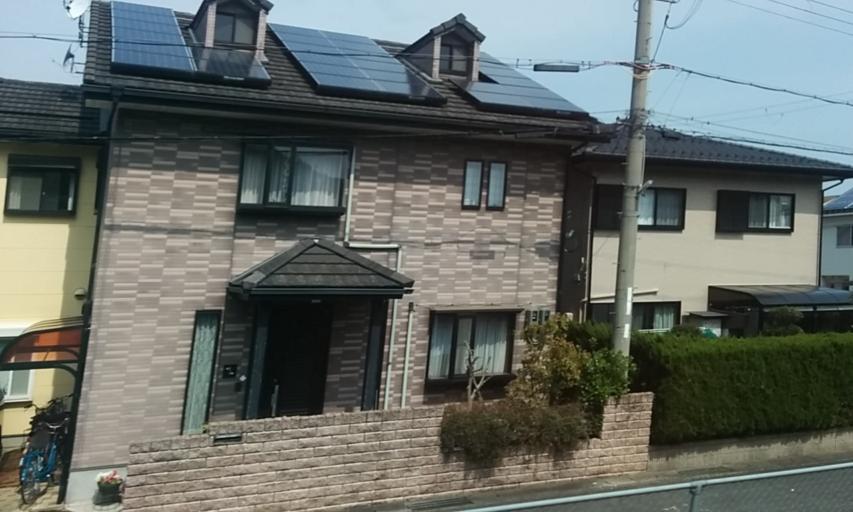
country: JP
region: Shiga Prefecture
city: Youkaichi
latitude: 35.1759
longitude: 136.1614
